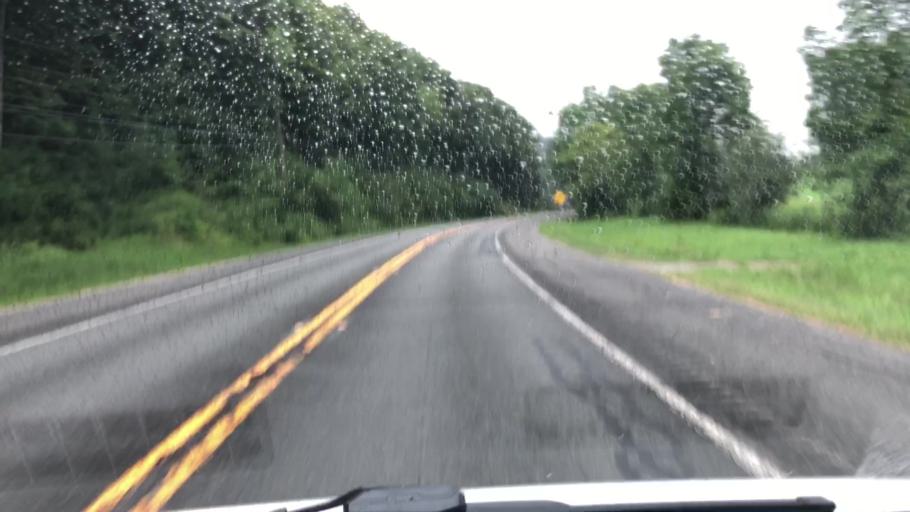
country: US
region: Massachusetts
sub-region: Berkshire County
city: Lanesborough
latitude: 42.5828
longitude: -73.2514
